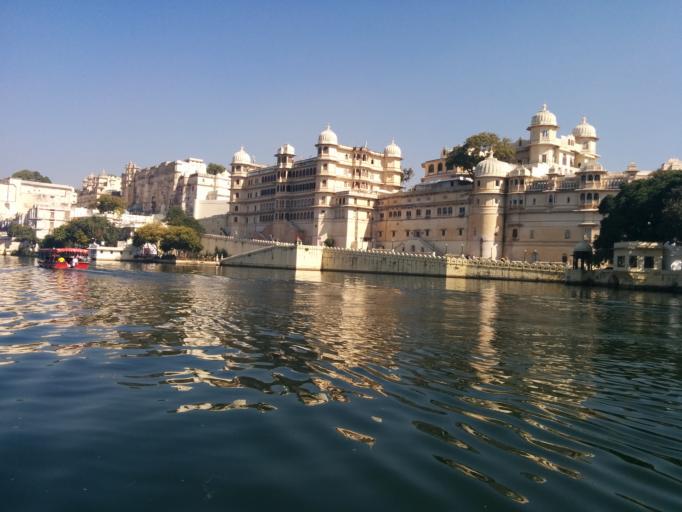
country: IN
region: Rajasthan
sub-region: Udaipur
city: Udaipur
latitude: 24.5735
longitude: 73.6823
